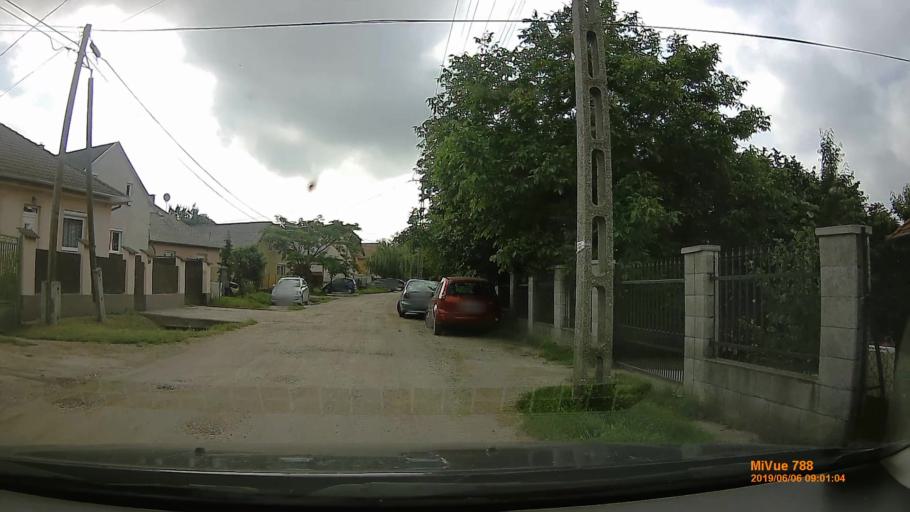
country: HU
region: Pest
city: Ecser
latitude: 47.4504
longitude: 19.3438
